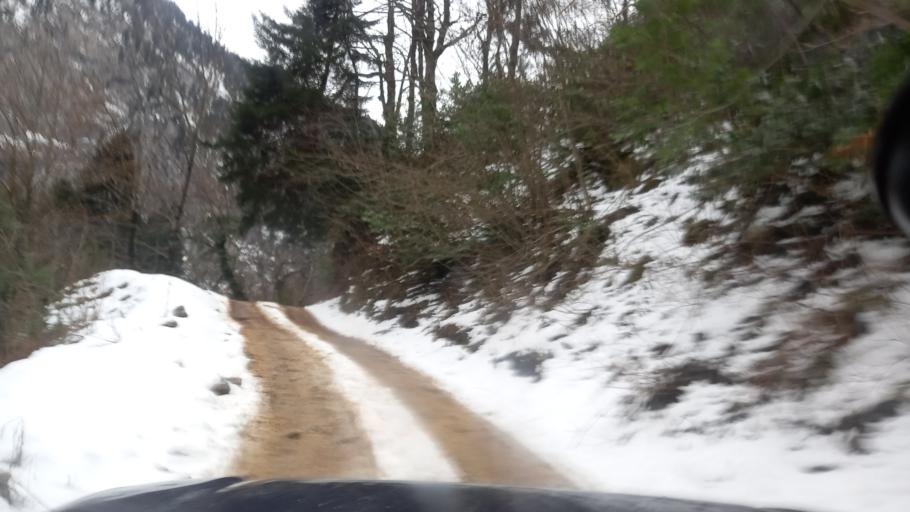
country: GE
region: Abkhazia
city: Gagra
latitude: 43.4347
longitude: 40.4428
